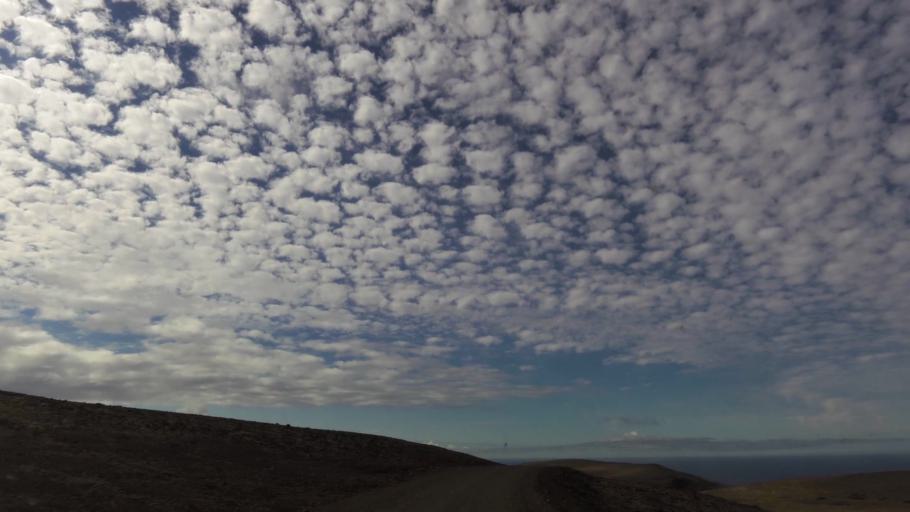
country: IS
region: West
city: Olafsvik
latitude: 65.6205
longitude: -24.2774
